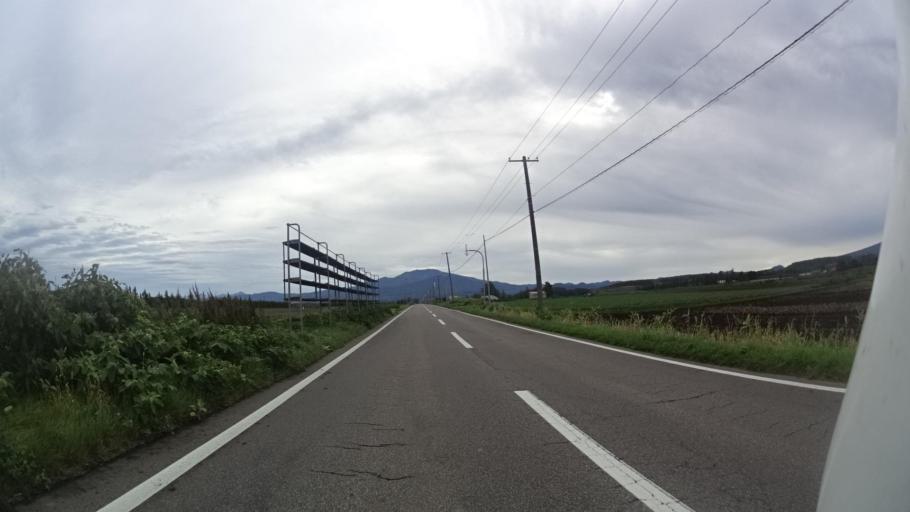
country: JP
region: Hokkaido
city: Abashiri
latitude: 43.8724
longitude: 144.6998
